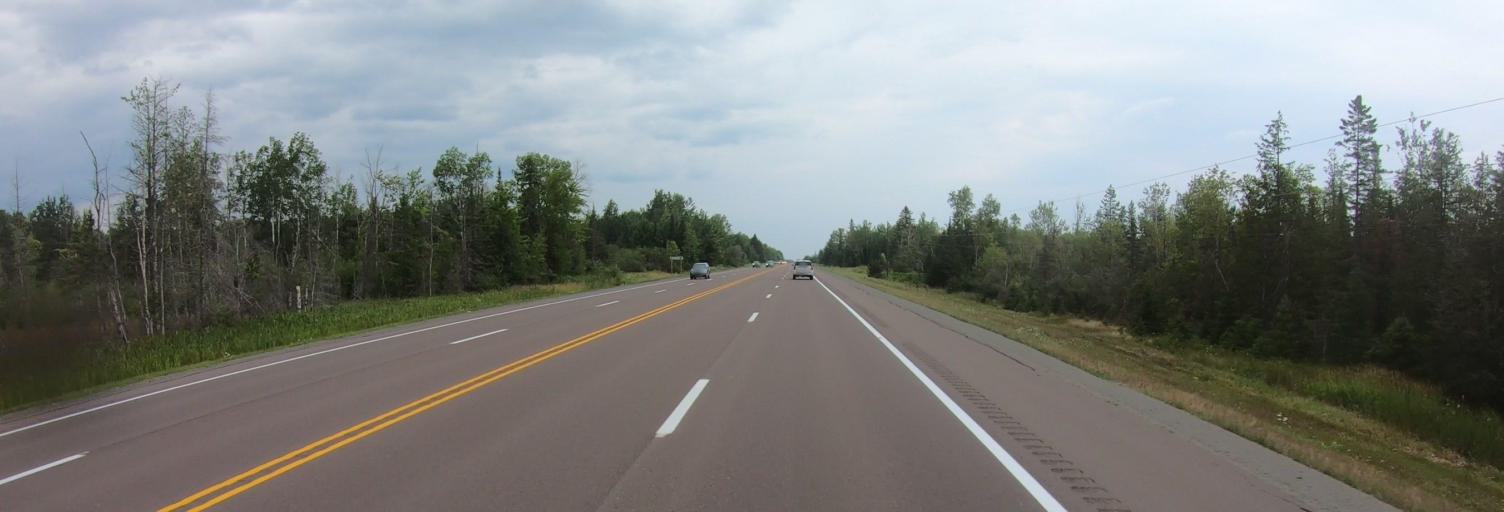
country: US
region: Michigan
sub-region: Baraga County
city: Baraga
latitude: 46.8947
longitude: -88.4762
